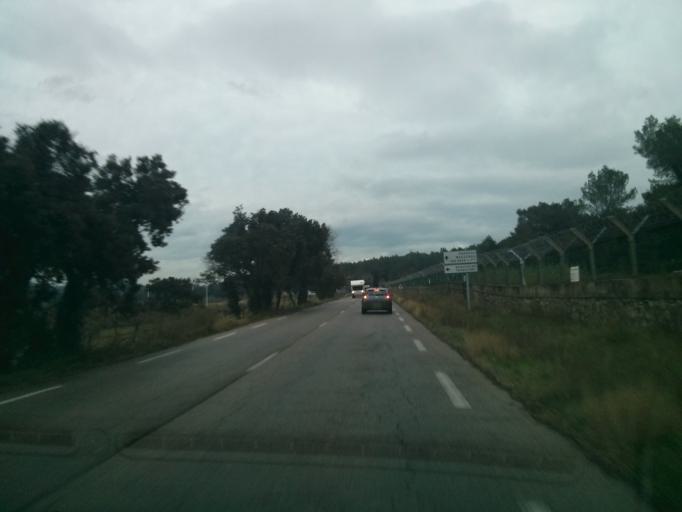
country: FR
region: Provence-Alpes-Cote d'Azur
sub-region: Departement des Bouches-du-Rhone
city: Fontvieille
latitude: 43.7294
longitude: 4.7349
